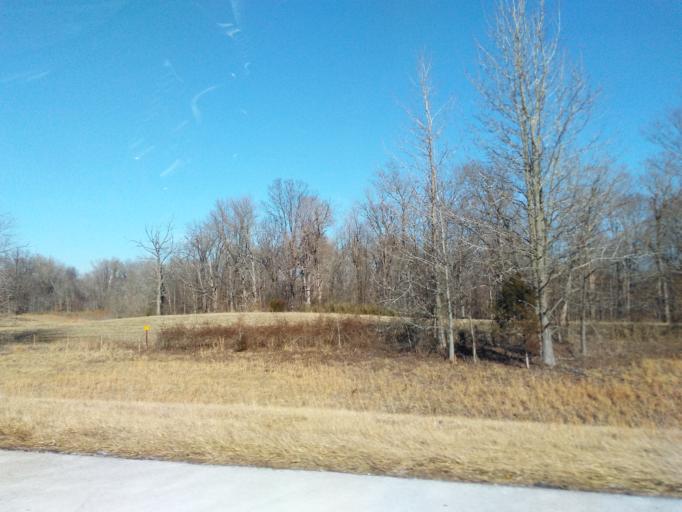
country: US
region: Illinois
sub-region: Johnson County
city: Vienna
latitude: 37.4284
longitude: -88.8771
